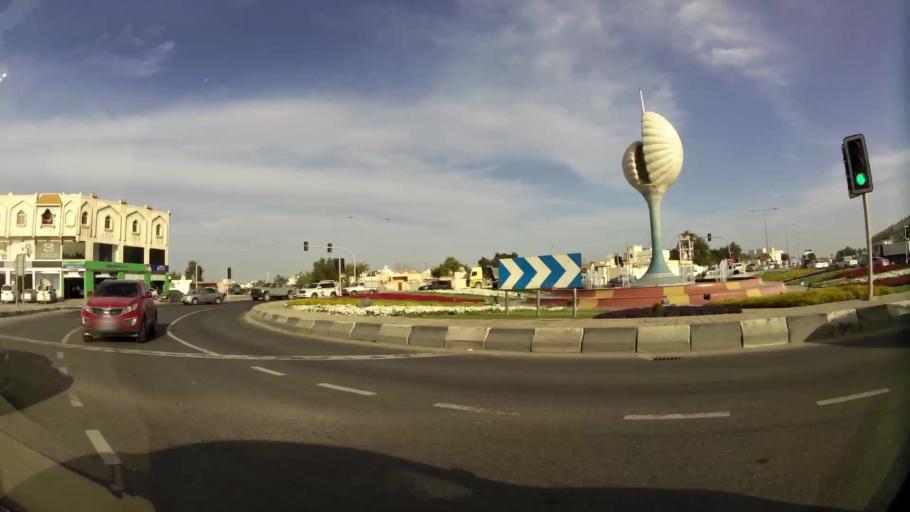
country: QA
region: Al Wakrah
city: Al Wakrah
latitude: 25.1773
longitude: 51.6044
